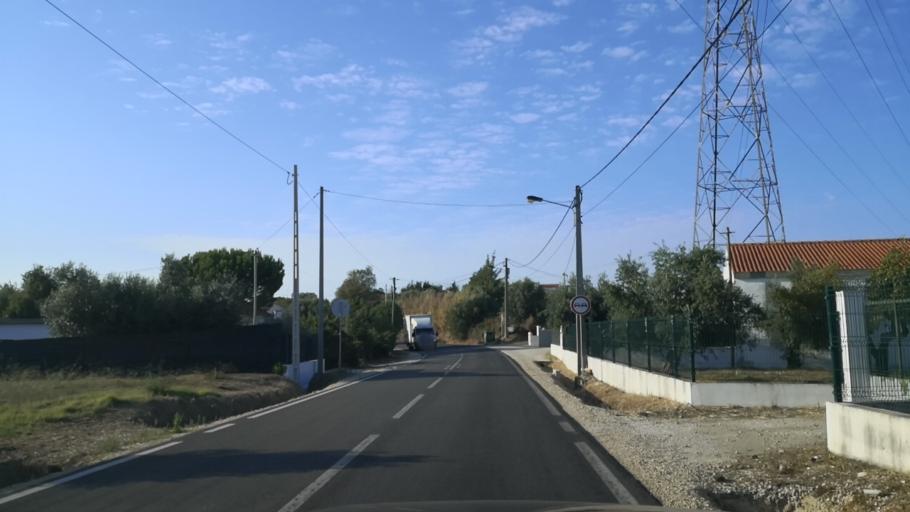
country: PT
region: Santarem
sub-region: Santarem
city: Santarem
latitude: 39.3051
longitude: -8.6603
